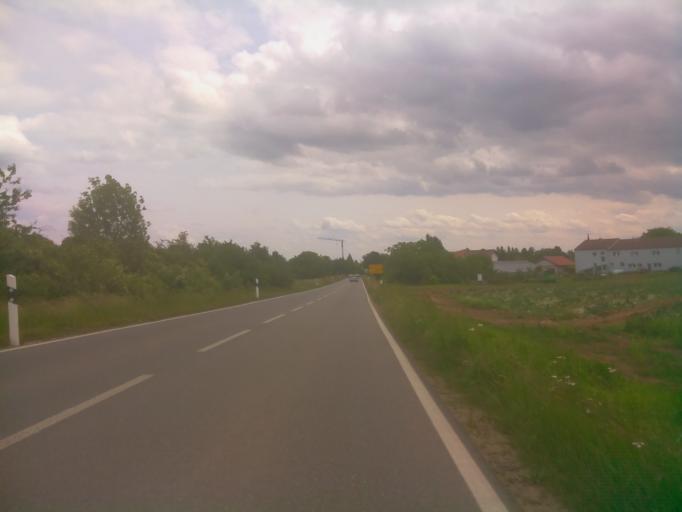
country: DE
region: Rheinland-Pfalz
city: Lambsheim
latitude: 49.5225
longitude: 8.2852
